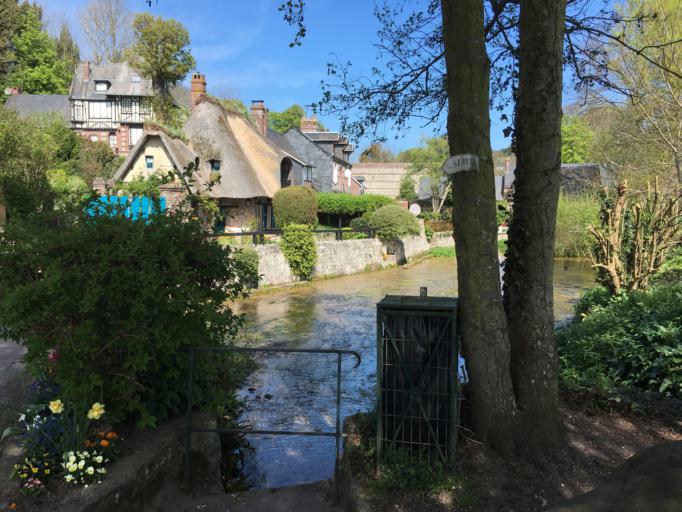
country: FR
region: Haute-Normandie
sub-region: Departement de la Seine-Maritime
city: Saint-Valery-en-Caux
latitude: 49.8699
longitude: 0.7989
